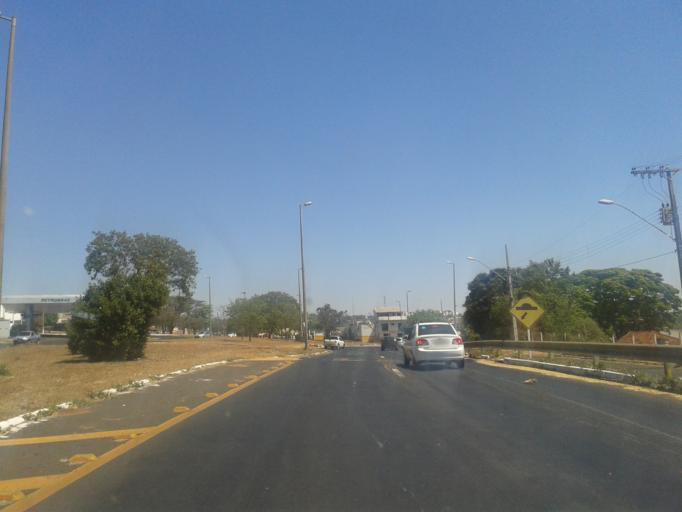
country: BR
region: Minas Gerais
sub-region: Uberlandia
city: Uberlandia
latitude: -18.9094
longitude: -48.3031
